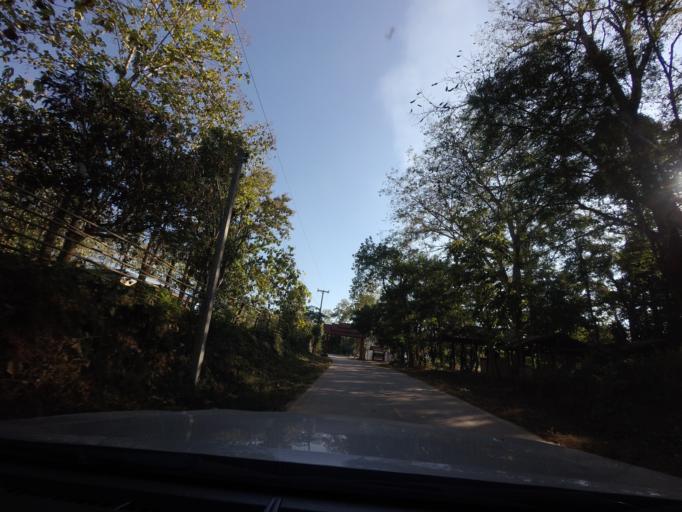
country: TH
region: Lampang
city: Chae Hom
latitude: 18.5955
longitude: 99.6269
